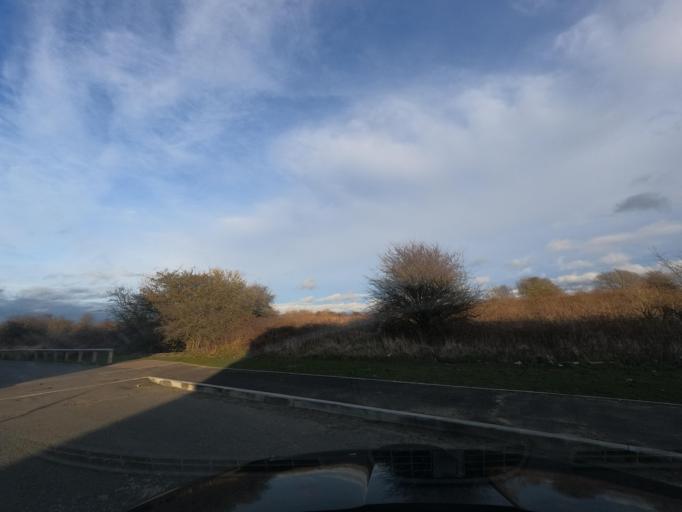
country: GB
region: England
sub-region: Northumberland
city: Cramlington
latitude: 55.0911
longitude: -1.5908
